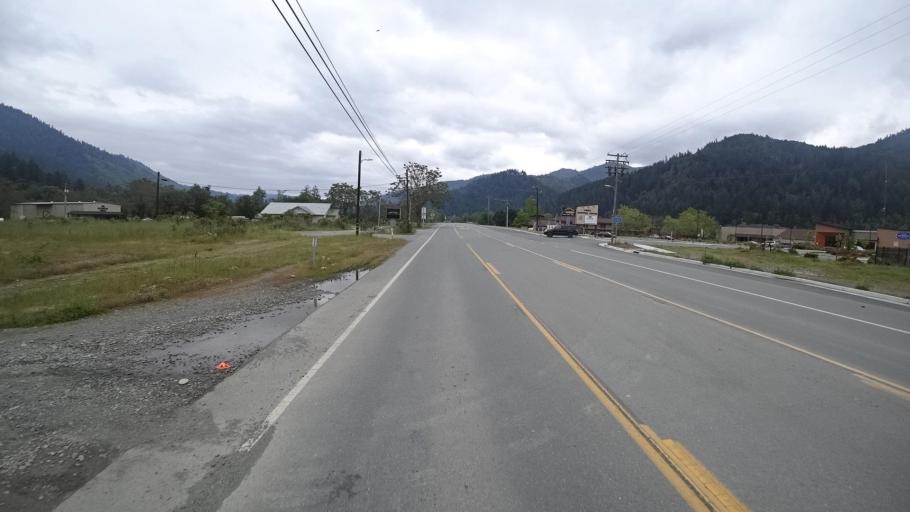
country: US
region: California
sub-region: Humboldt County
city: Willow Creek
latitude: 41.0636
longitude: -123.6857
